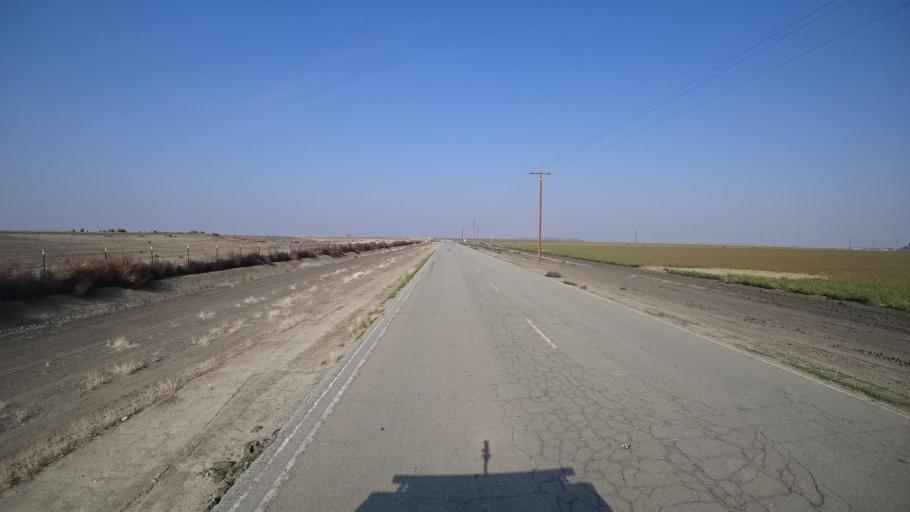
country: US
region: California
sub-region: Kern County
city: Buttonwillow
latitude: 35.3310
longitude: -119.3767
